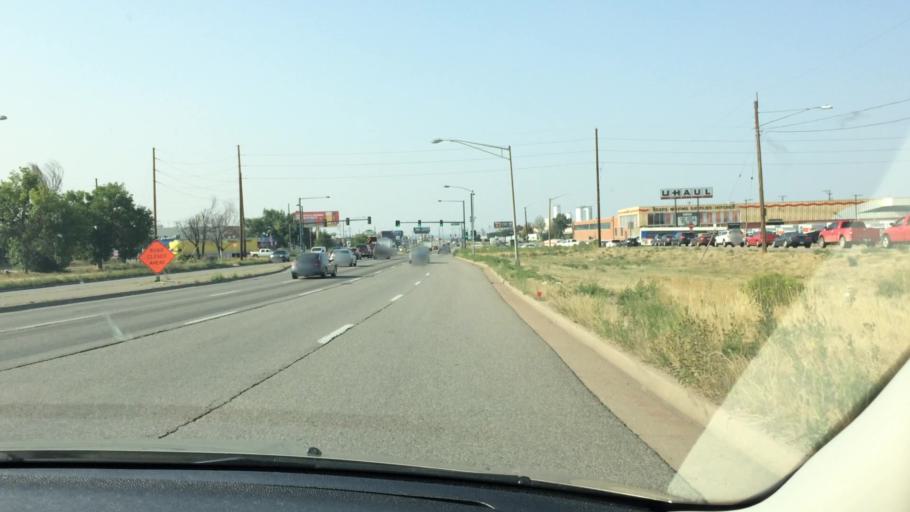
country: US
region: Colorado
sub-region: Adams County
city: Commerce City
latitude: 39.7823
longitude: -104.9404
